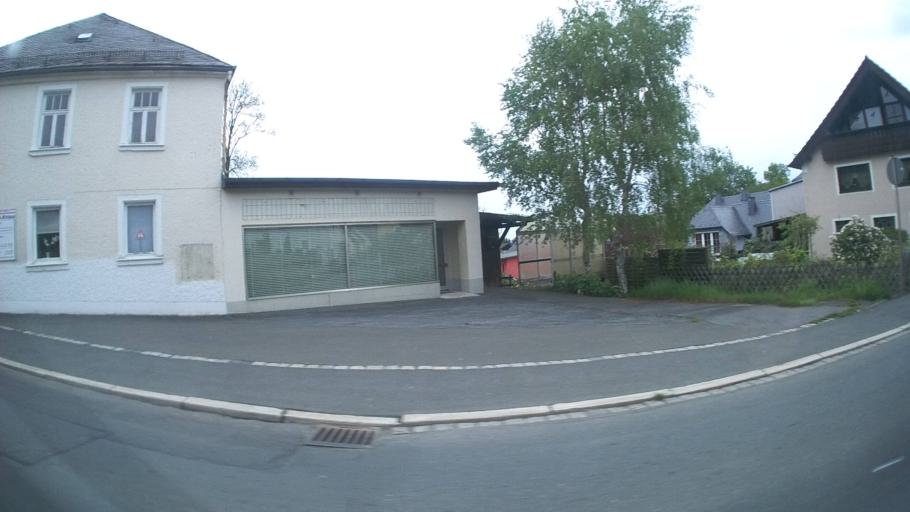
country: DE
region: Bavaria
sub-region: Upper Franconia
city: Sparneck
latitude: 50.1612
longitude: 11.8418
